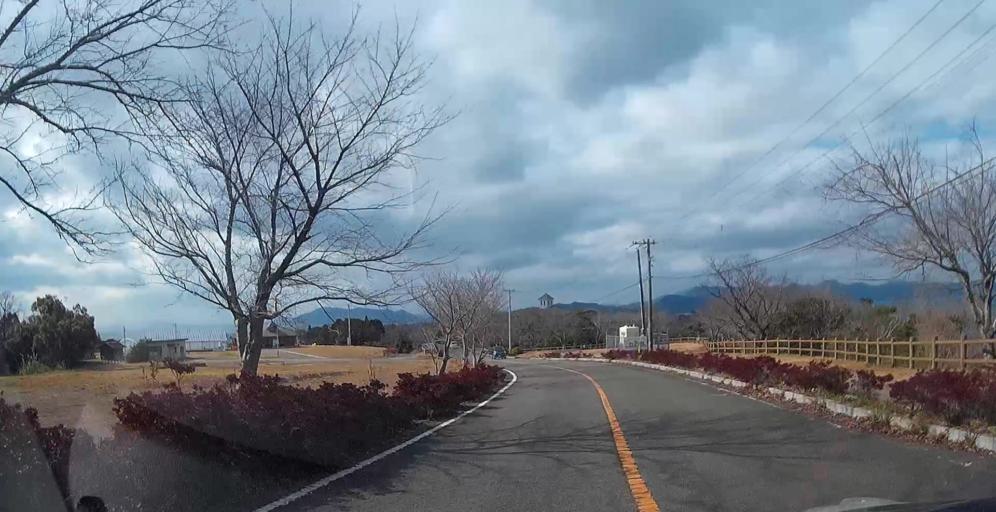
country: JP
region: Kumamoto
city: Yatsushiro
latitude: 32.3668
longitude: 130.4949
